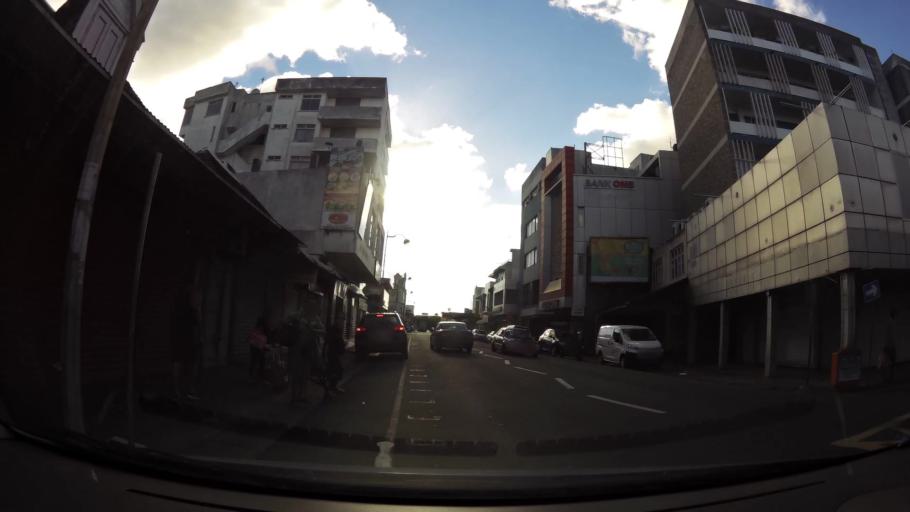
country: MU
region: Plaines Wilhems
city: Ebene
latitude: -20.2427
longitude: 57.4747
